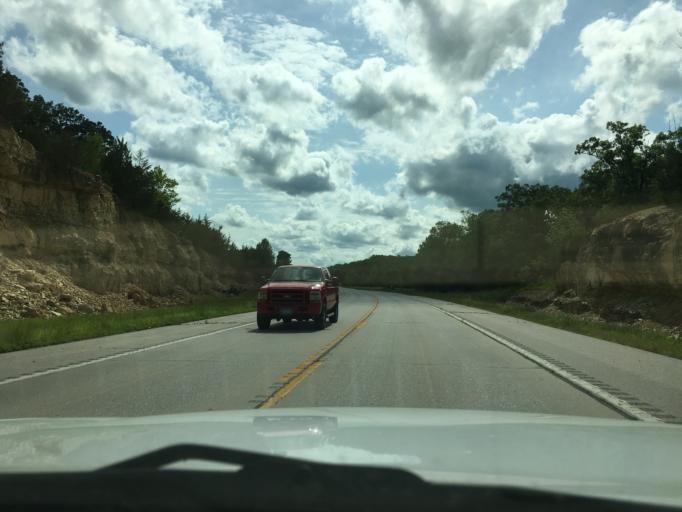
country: US
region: Missouri
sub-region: Franklin County
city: Gerald
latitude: 38.4231
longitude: -91.2794
